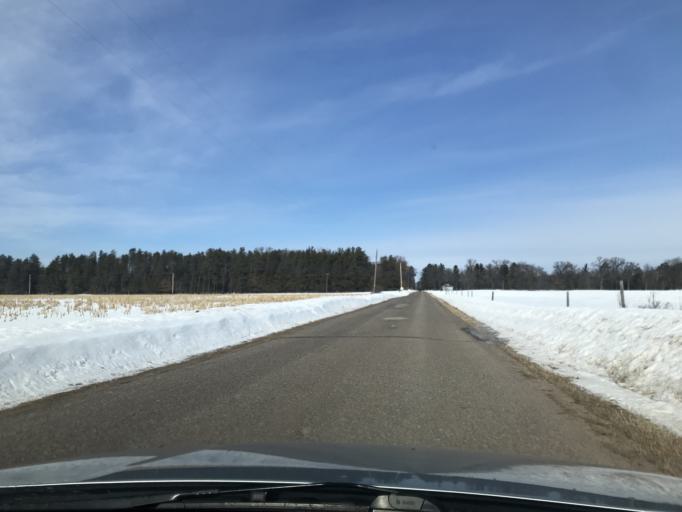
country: US
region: Wisconsin
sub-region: Marinette County
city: Peshtigo
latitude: 45.2187
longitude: -87.9626
